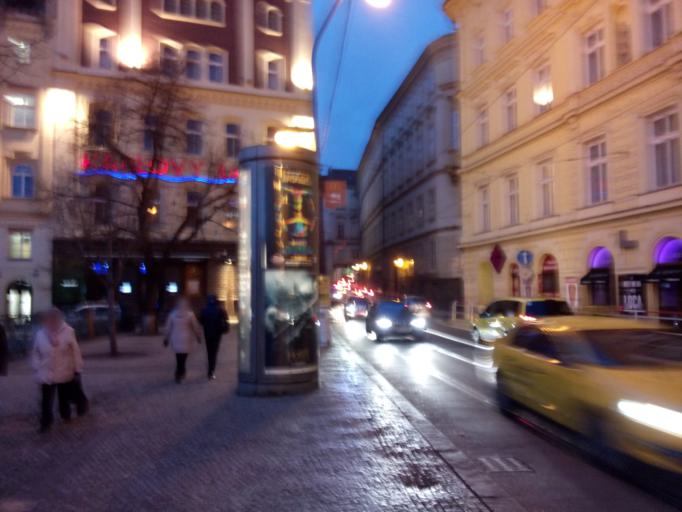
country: CZ
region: Praha
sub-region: Praha 1
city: Stare Mesto
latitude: 50.0853
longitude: 14.4138
